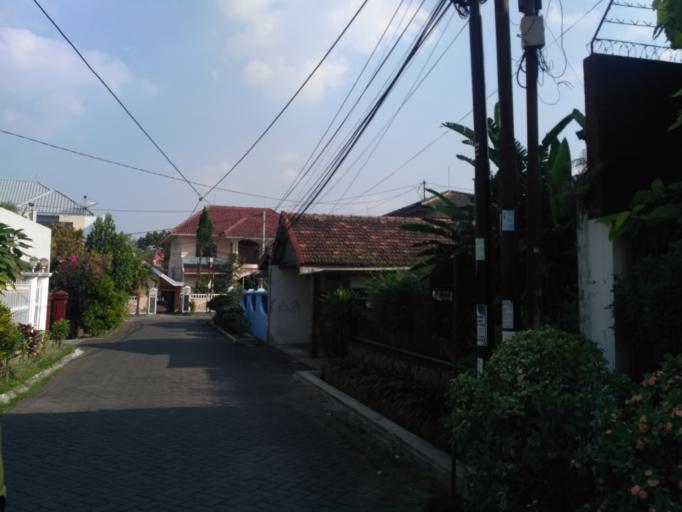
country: ID
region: East Java
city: Malang
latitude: -7.9566
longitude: 112.6097
